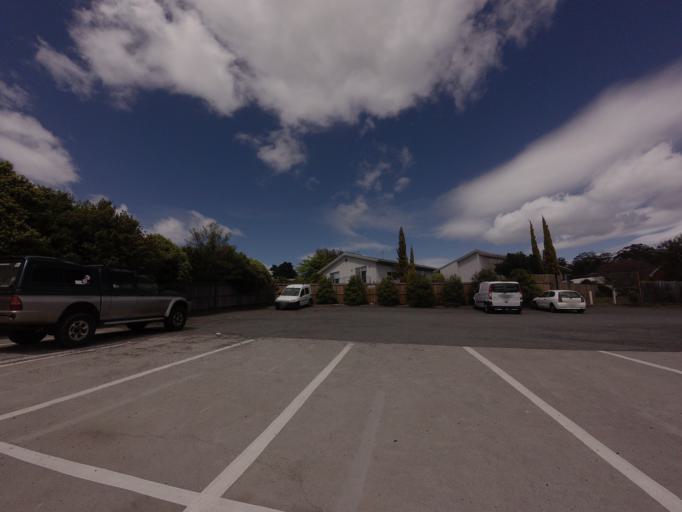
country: AU
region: Tasmania
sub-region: Clarence
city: Howrah
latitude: -42.8888
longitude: 147.4232
